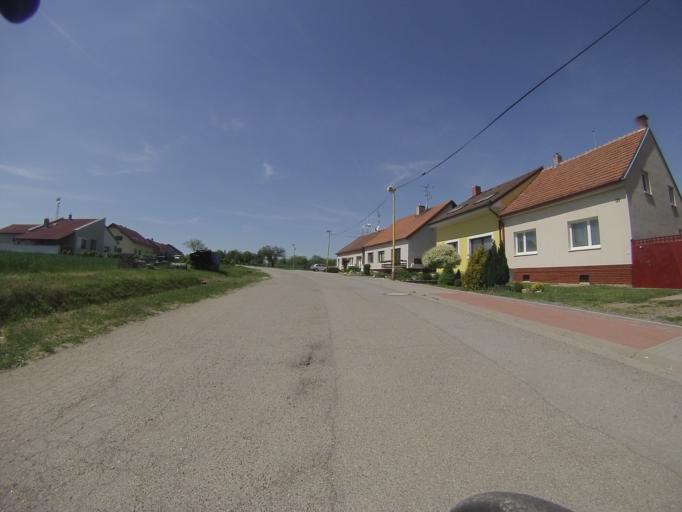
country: CZ
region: South Moravian
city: Vranovice
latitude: 48.9674
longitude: 16.5959
